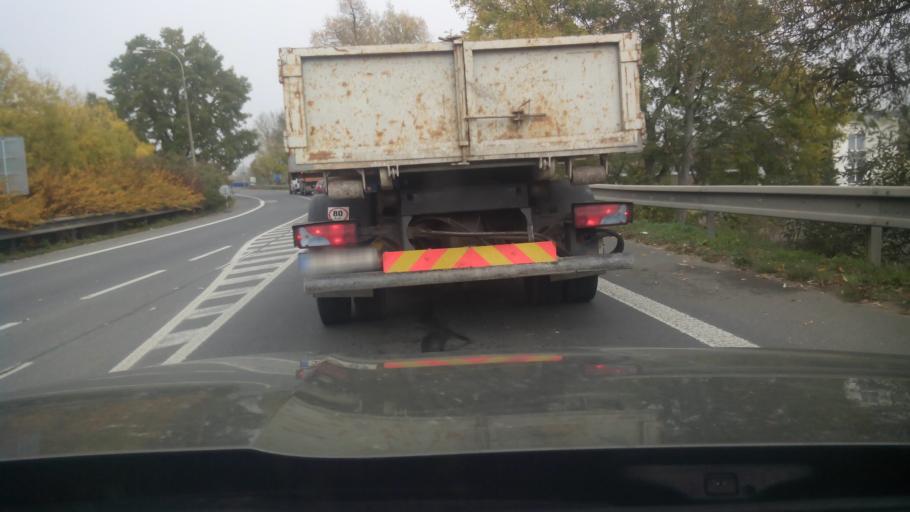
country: CZ
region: Jihocesky
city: Strakonice
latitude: 49.2636
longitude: 13.9158
